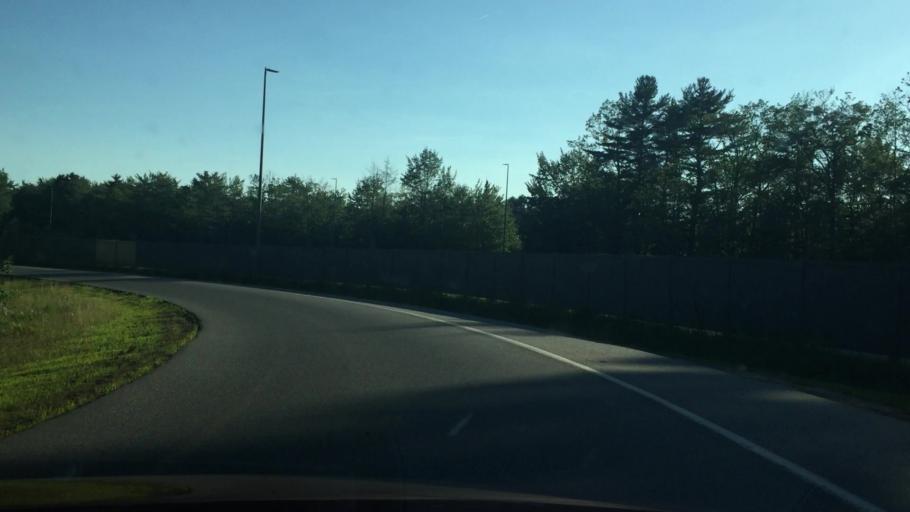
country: US
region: Maine
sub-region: Cumberland County
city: Yarmouth
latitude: 43.7858
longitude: -70.1915
